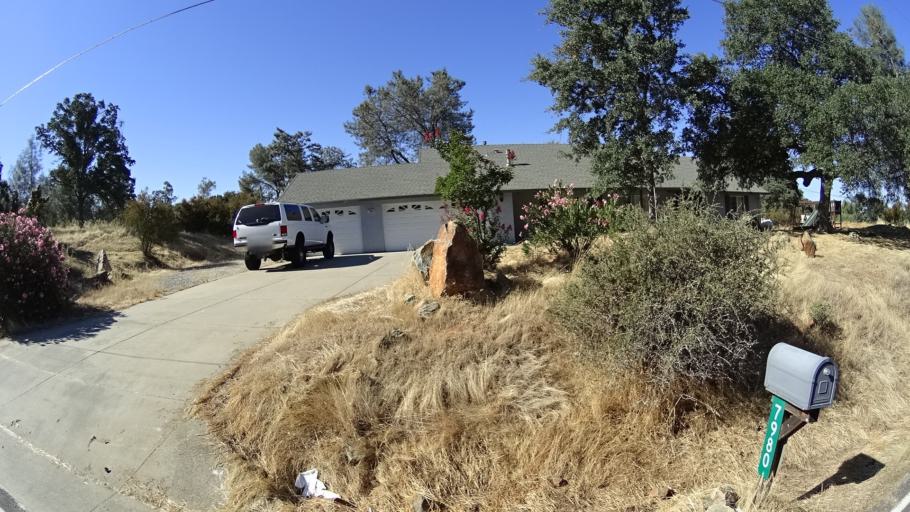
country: US
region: California
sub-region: Calaveras County
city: Rancho Calaveras
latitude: 38.1047
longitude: -120.8642
